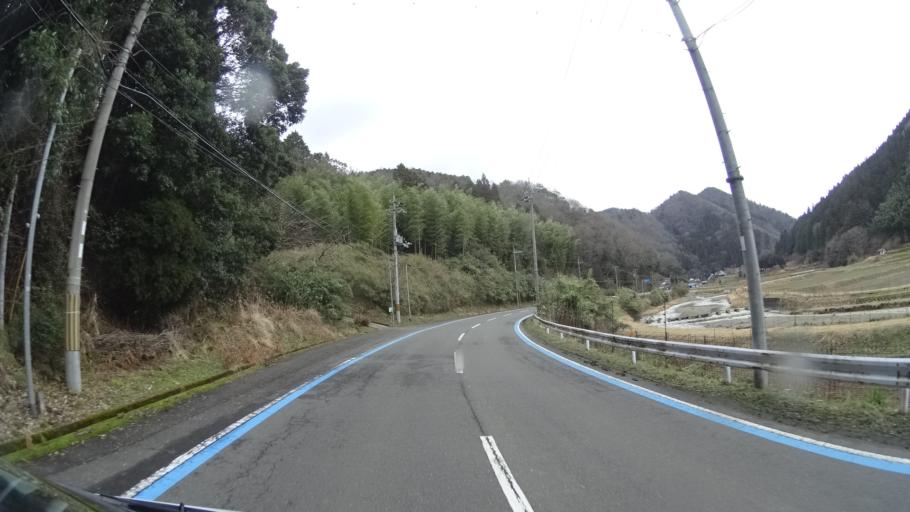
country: JP
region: Kyoto
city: Maizuru
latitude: 35.4037
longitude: 135.4155
